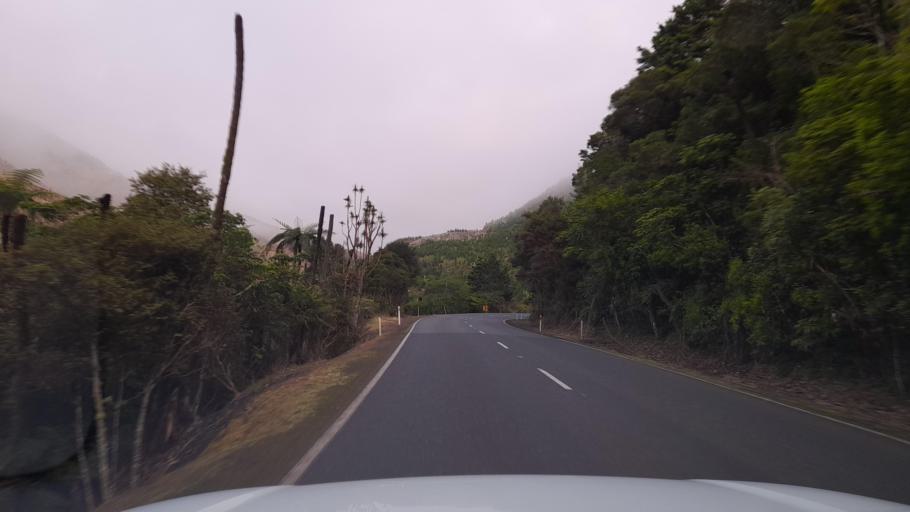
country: NZ
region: Northland
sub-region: Far North District
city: Moerewa
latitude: -35.6151
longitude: 173.8425
